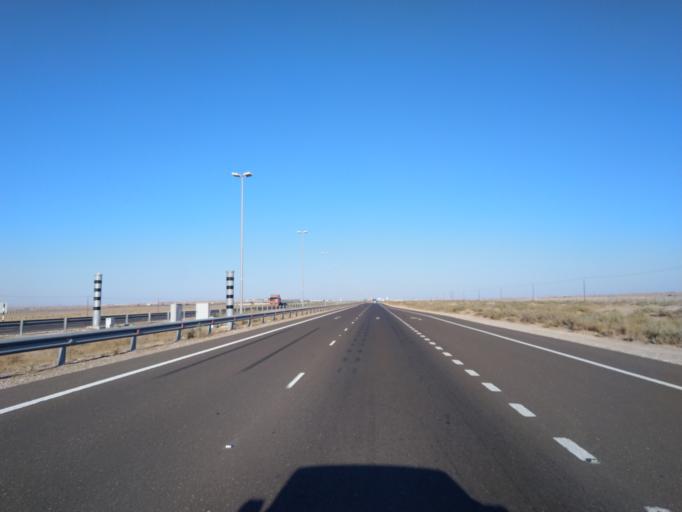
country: OM
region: Al Buraimi
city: Al Buraymi
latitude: 24.4978
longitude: 55.4349
